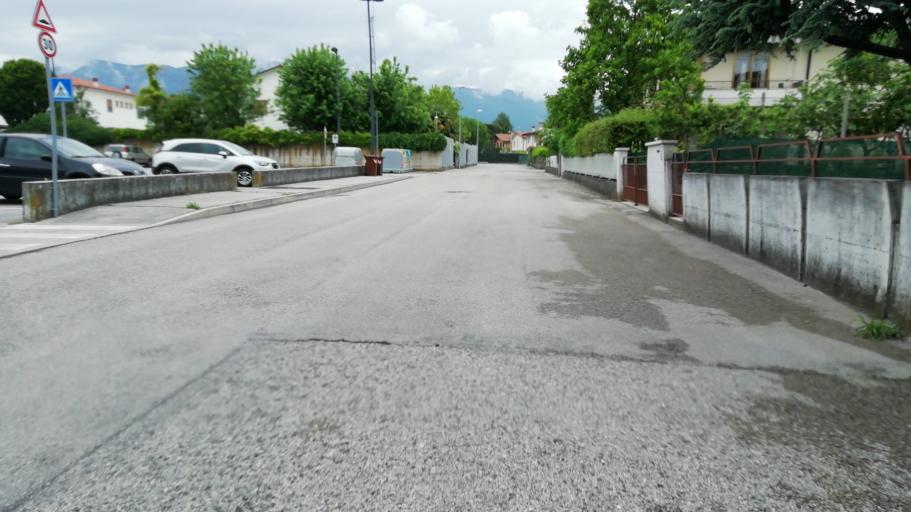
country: IT
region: Veneto
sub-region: Provincia di Vicenza
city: Thiene
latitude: 45.7132
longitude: 11.4783
